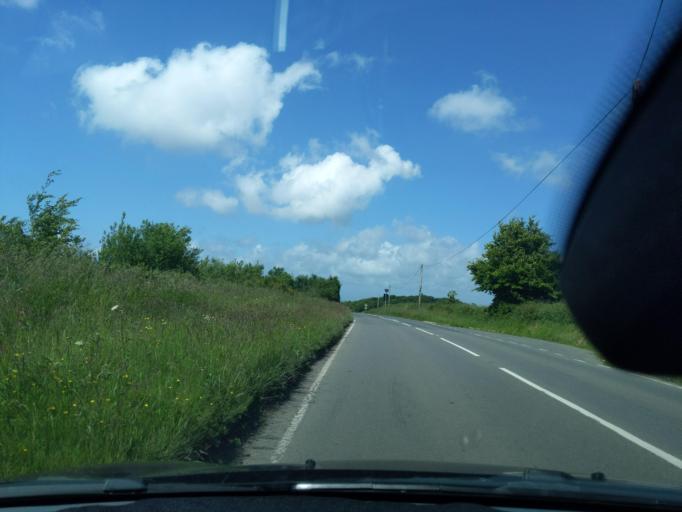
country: GB
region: England
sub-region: Devon
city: Great Torrington
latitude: 50.9793
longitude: -4.0954
